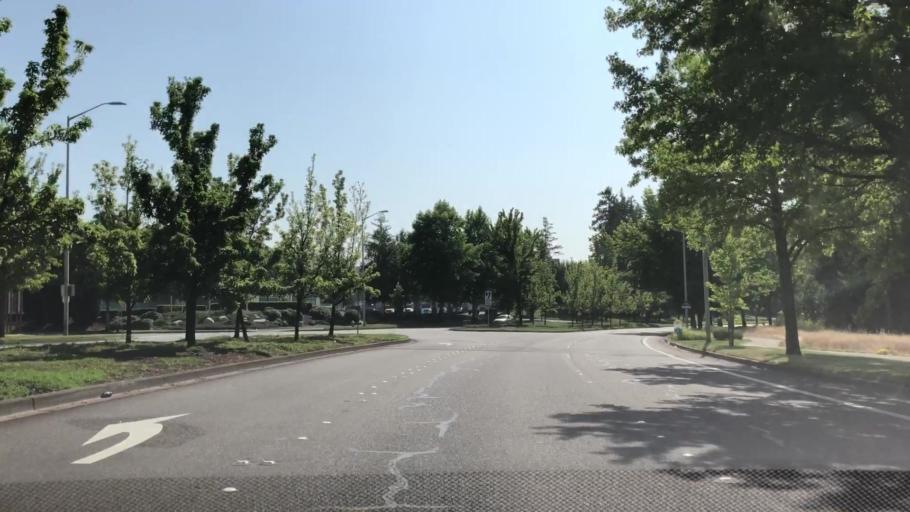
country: US
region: Washington
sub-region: Thurston County
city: Tanglewilde-Thompson Place
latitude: 47.0728
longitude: -122.7514
